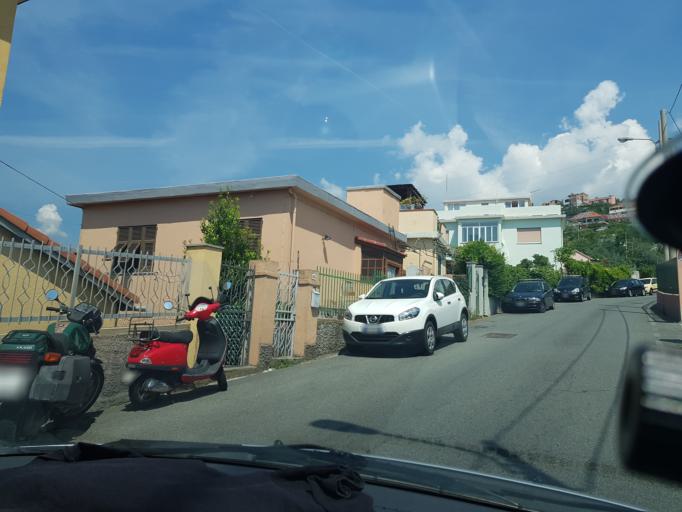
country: IT
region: Liguria
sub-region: Provincia di Genova
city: San Teodoro
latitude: 44.4364
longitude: 8.8395
